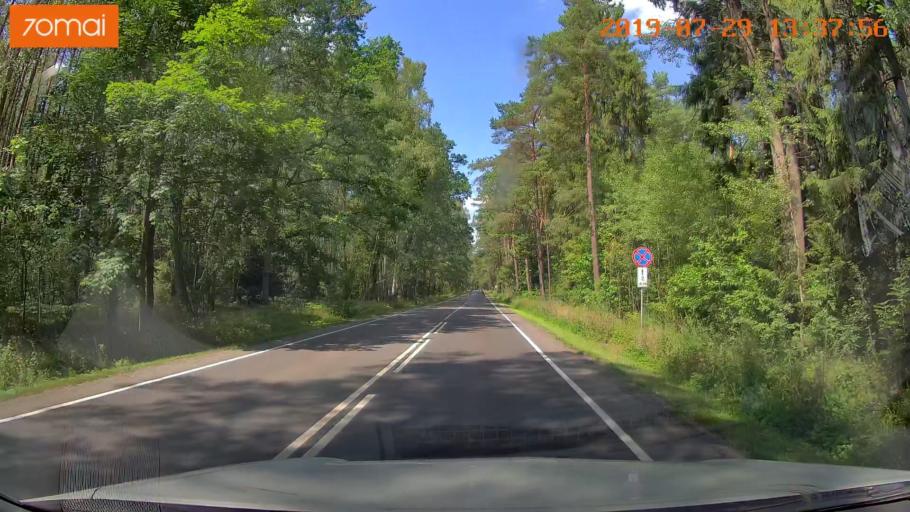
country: RU
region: Kaliningrad
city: Volochayevskoye
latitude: 54.7173
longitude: 20.1776
